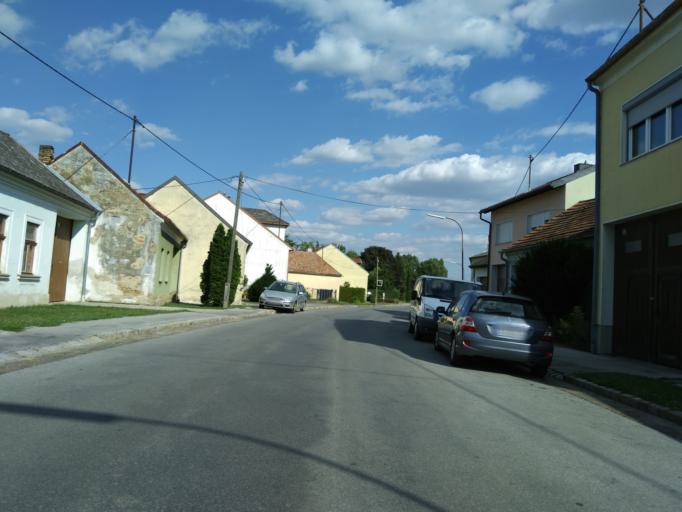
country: AT
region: Lower Austria
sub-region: Politischer Bezirk Mistelbach
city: Gross-Engersdorf
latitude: 48.3556
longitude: 16.5797
